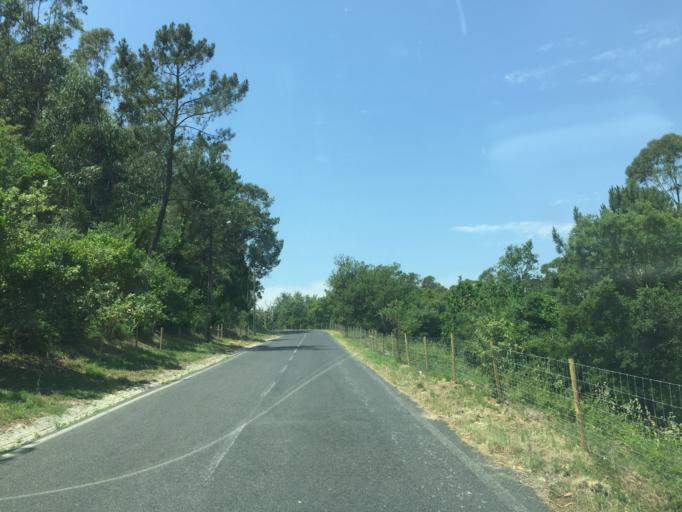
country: PT
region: Lisbon
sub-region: Mafra
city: Milharado
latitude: 38.8999
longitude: -9.1821
